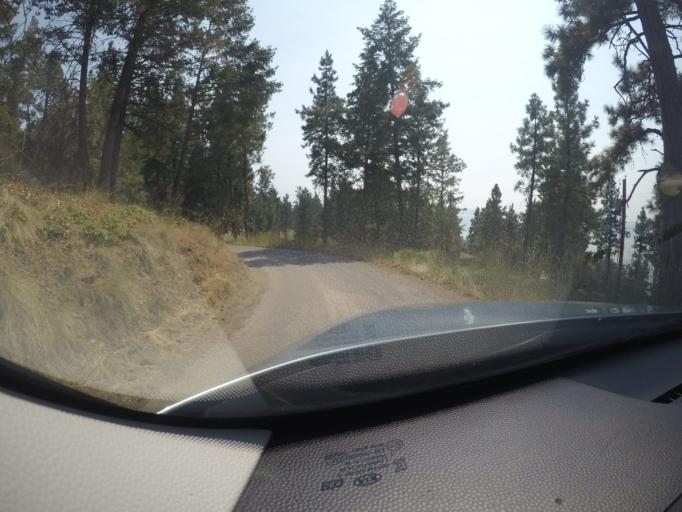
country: US
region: Montana
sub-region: Lake County
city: Polson
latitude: 47.7586
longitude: -114.1435
